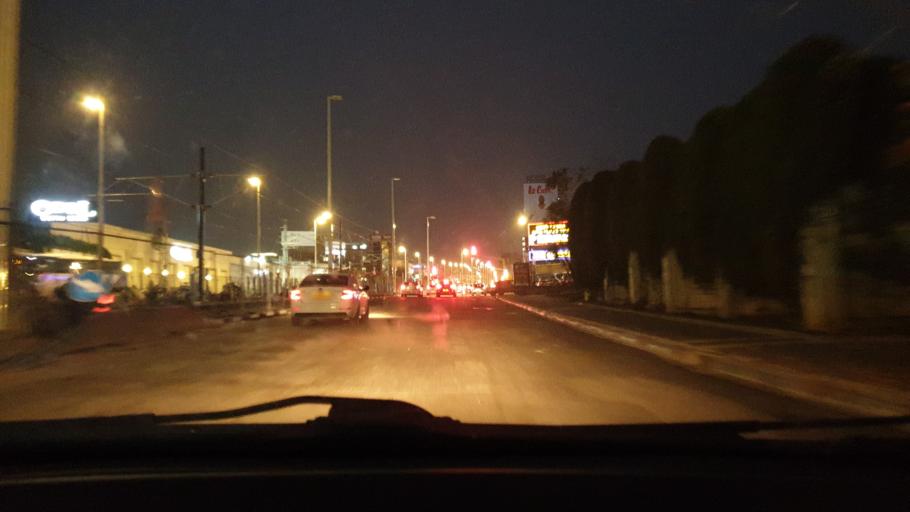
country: IL
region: Tel Aviv
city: Giv`at Shemu'el
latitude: 32.0925
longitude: 34.8524
